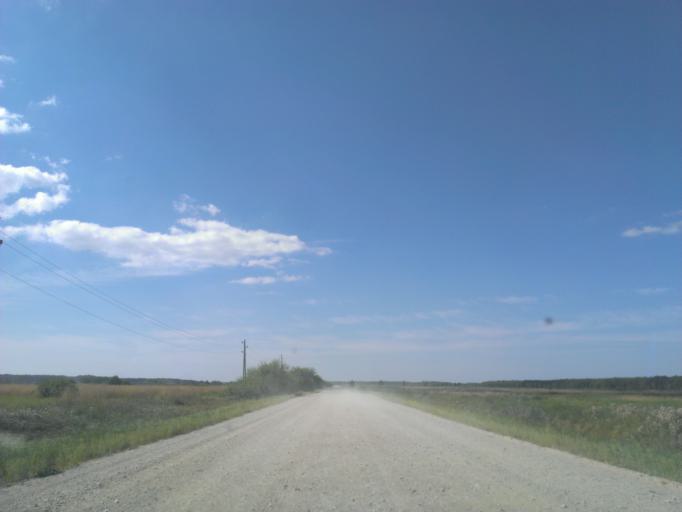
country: LV
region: Carnikava
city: Carnikava
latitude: 57.0824
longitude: 24.2403
